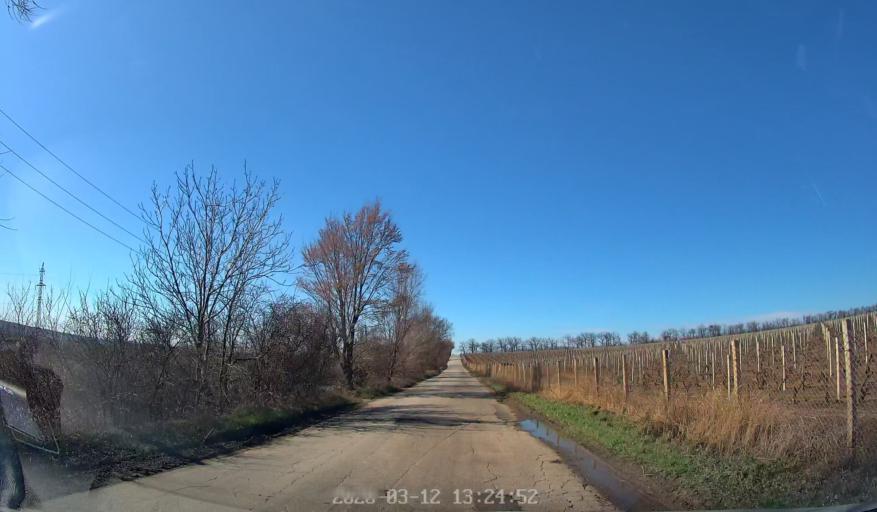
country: MD
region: Laloveni
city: Ialoveni
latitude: 46.9413
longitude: 28.8248
